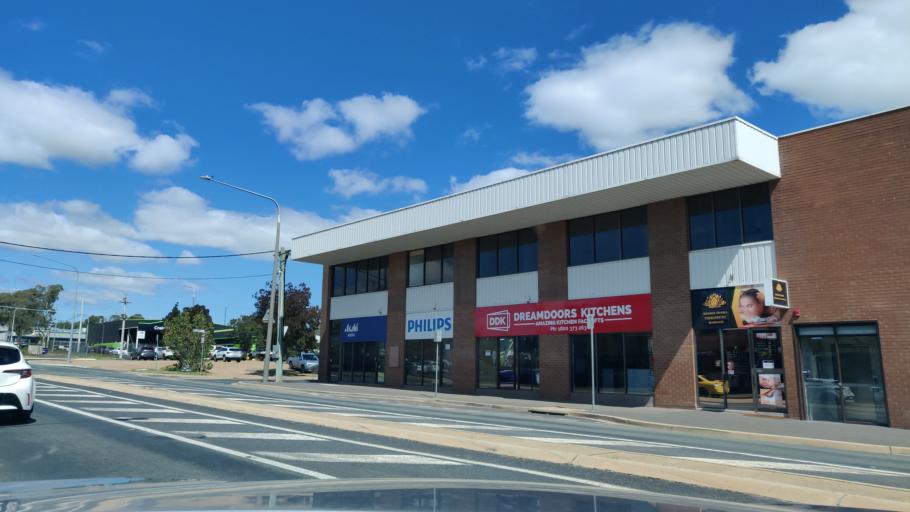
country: AU
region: Australian Capital Territory
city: Forrest
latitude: -35.3544
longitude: 149.0889
